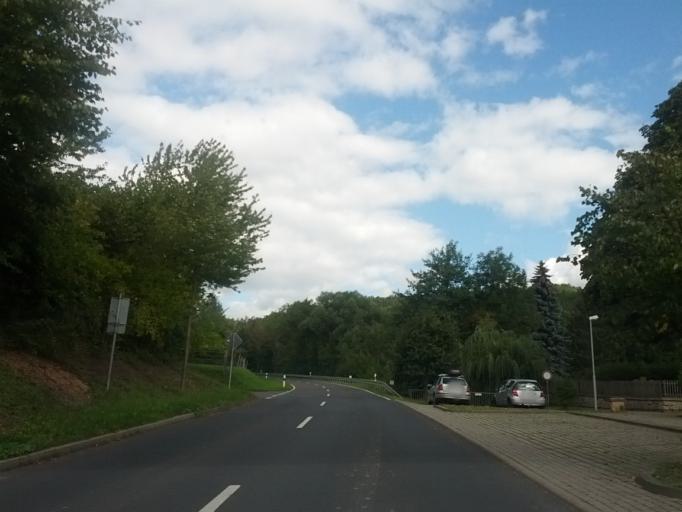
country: DE
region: Hesse
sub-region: Regierungsbezirk Kassel
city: Herleshausen
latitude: 51.0080
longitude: 10.1610
